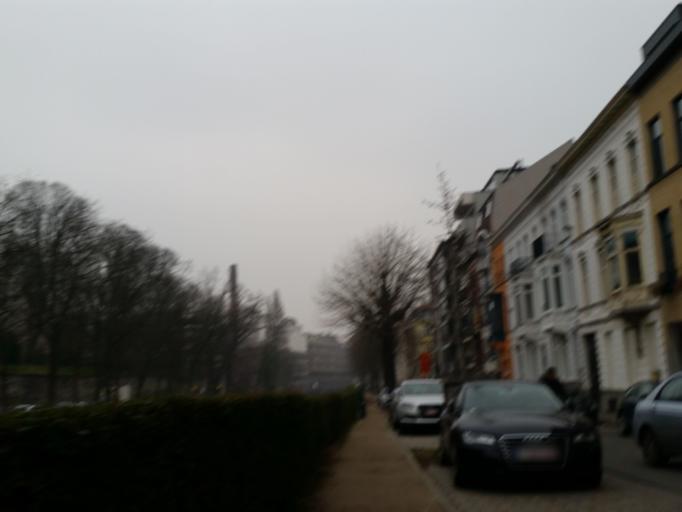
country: BE
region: Flanders
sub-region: Provincie Oost-Vlaanderen
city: Gent
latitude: 51.0418
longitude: 3.7294
